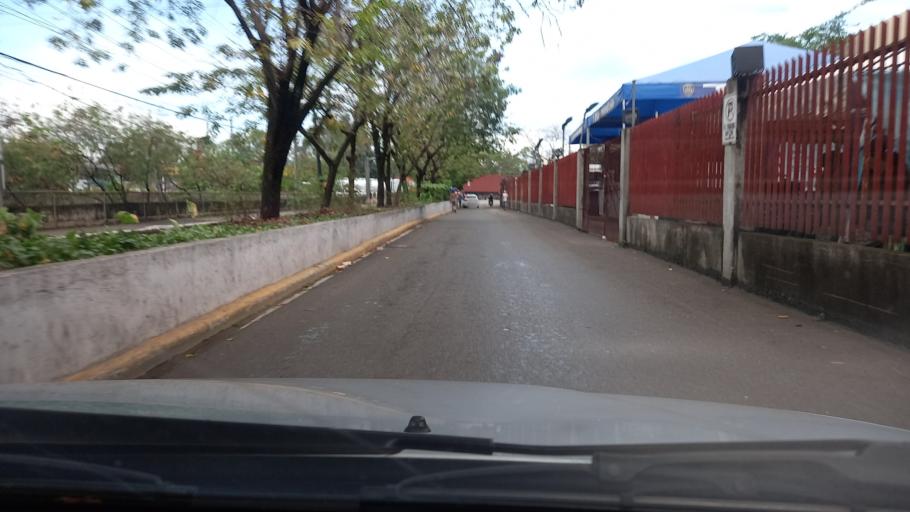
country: PH
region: Central Visayas
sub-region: Lapu-Lapu City
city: Buagsong
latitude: 10.3237
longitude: 123.9409
